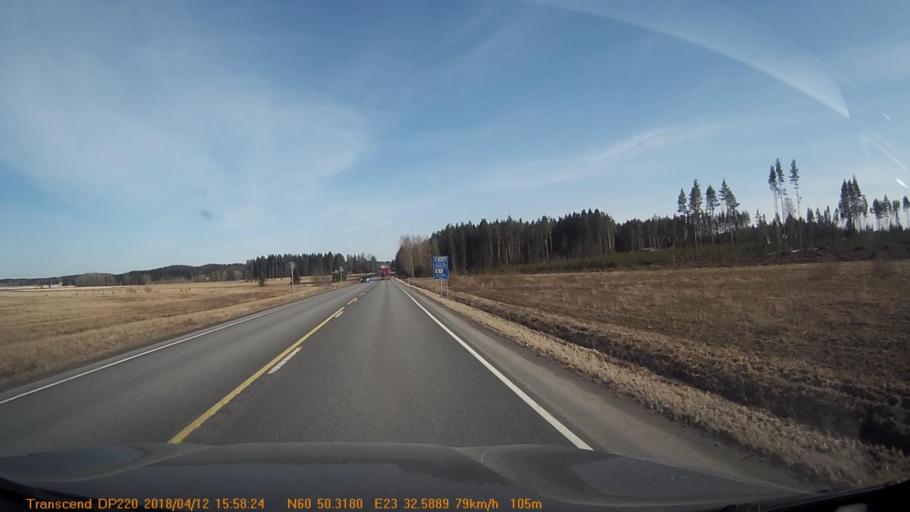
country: FI
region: Haeme
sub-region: Forssa
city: Jokioinen
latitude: 60.8381
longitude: 23.5445
